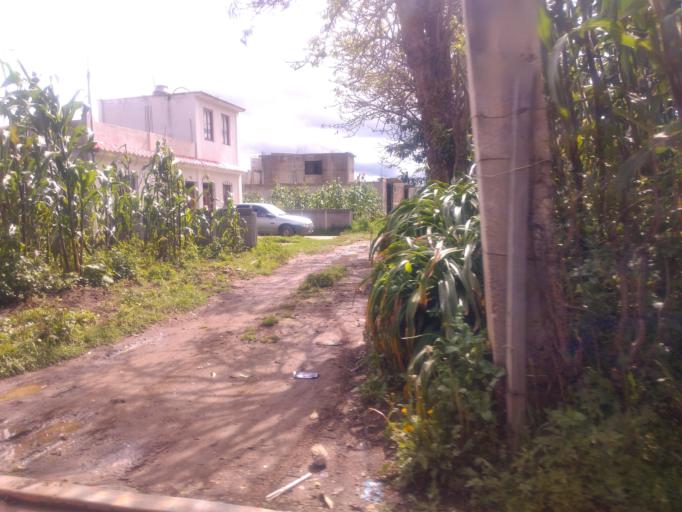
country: GT
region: Quetzaltenango
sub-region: Municipio de La Esperanza
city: La Esperanza
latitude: 14.8589
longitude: -91.5701
